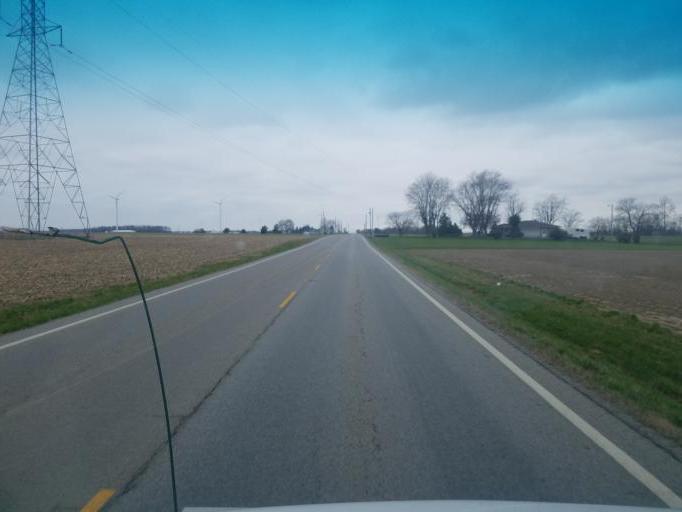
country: US
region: Ohio
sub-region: Van Wert County
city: Van Wert
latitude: 40.9294
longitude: -84.5217
